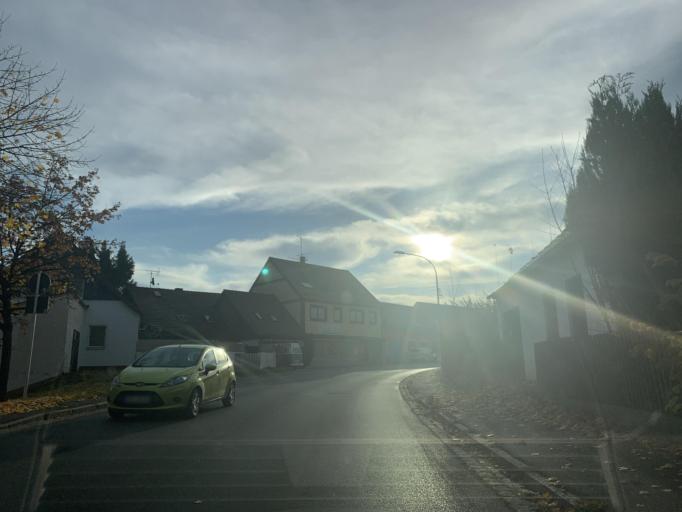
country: DE
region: Bavaria
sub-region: Upper Palatinate
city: Neunburg vorm Wald
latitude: 49.3467
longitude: 12.3900
